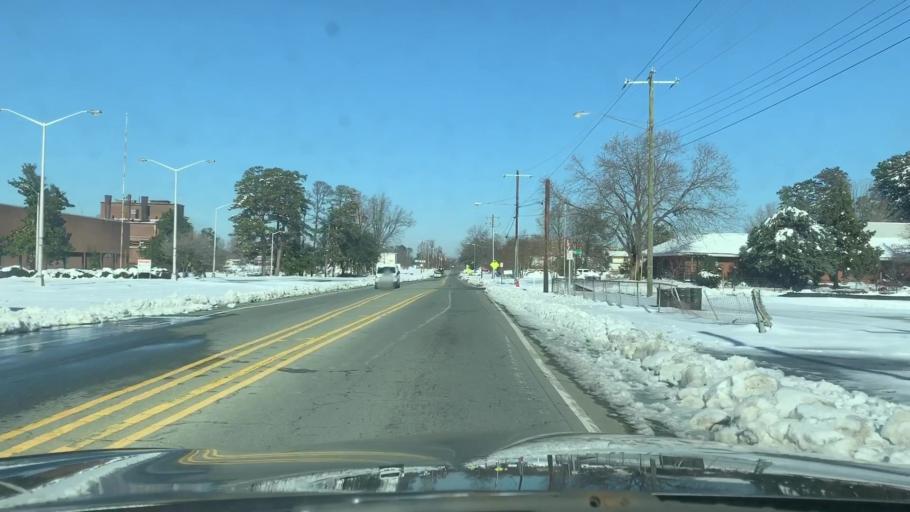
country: US
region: North Carolina
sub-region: Alamance County
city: Graham
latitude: 36.0966
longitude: -79.4060
